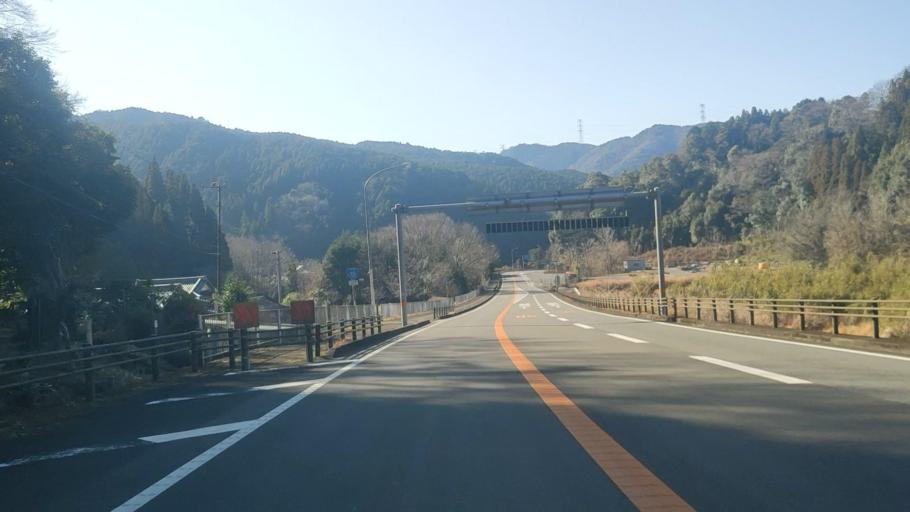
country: JP
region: Oita
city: Tsukumiura
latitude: 32.9967
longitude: 131.7641
